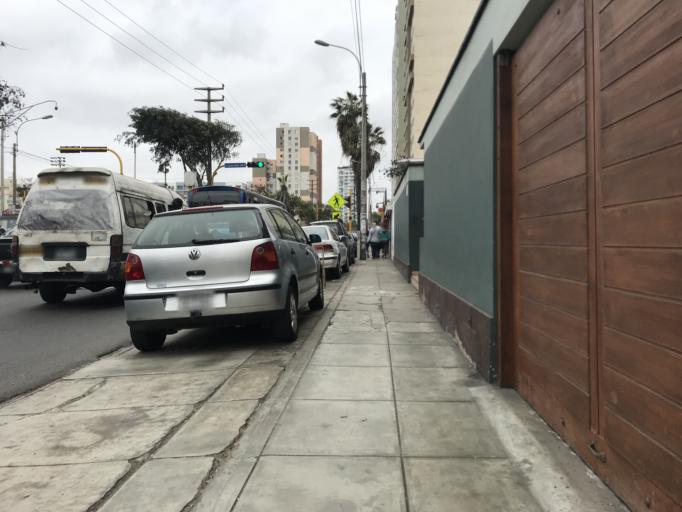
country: PE
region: Callao
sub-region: Callao
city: Callao
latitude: -12.0753
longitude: -77.0779
